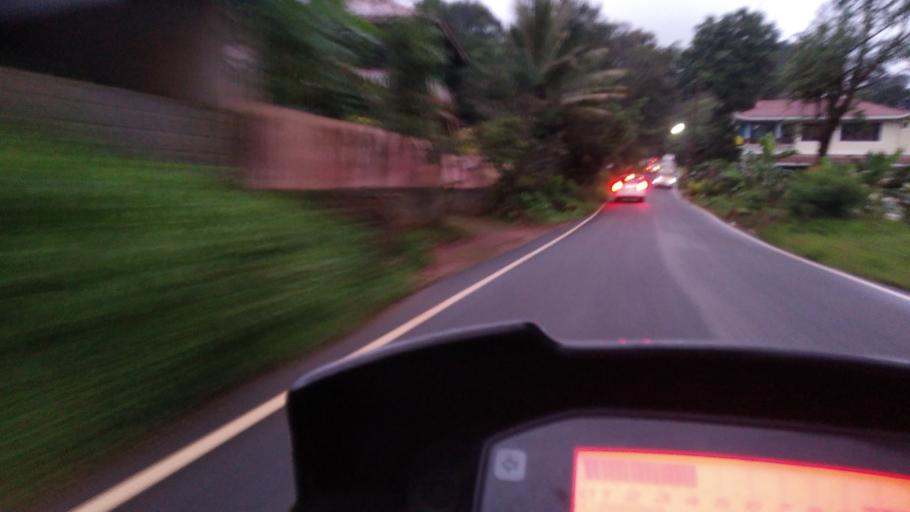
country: IN
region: Kerala
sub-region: Idukki
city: Munnar
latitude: 9.9583
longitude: 77.0887
